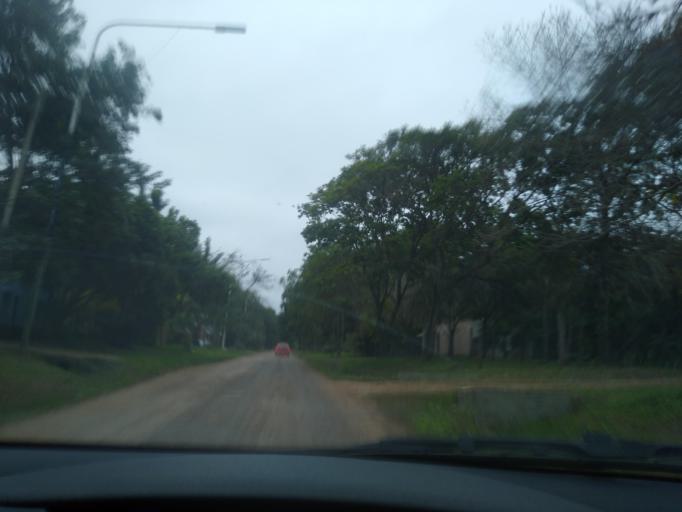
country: AR
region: Chaco
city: Colonia Benitez
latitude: -27.3343
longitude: -58.9555
